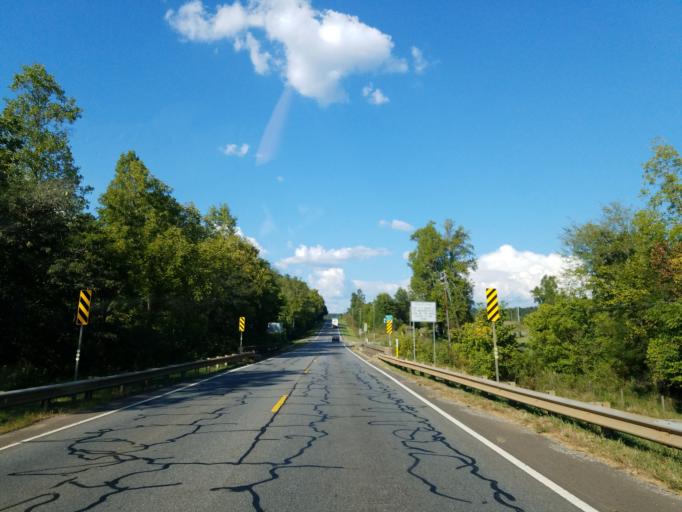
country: US
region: Georgia
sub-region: Bartow County
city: Rydal
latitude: 34.3691
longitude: -84.7127
